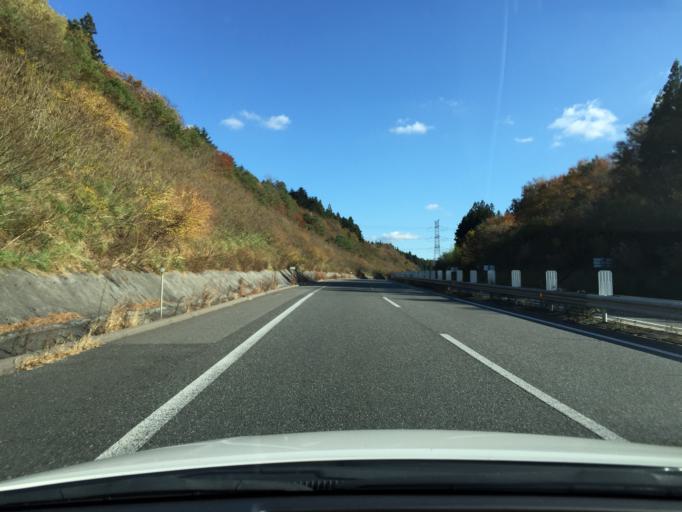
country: JP
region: Fukushima
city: Funehikimachi-funehiki
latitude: 37.2439
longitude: 140.6713
